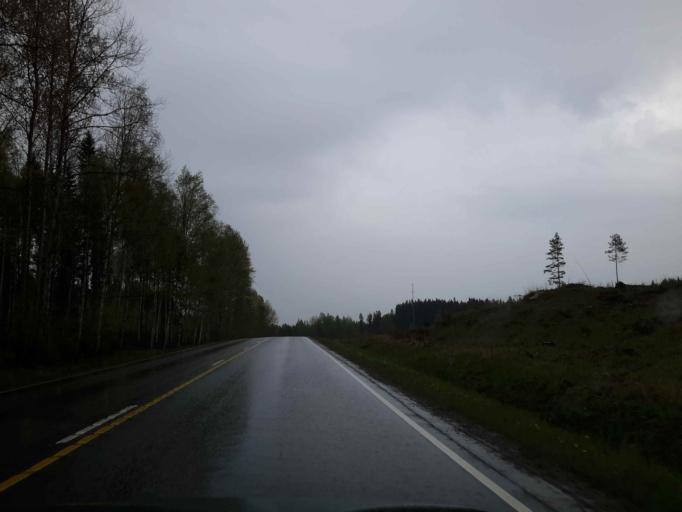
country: FI
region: Uusimaa
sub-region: Helsinki
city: Vihti
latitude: 60.3908
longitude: 24.4978
